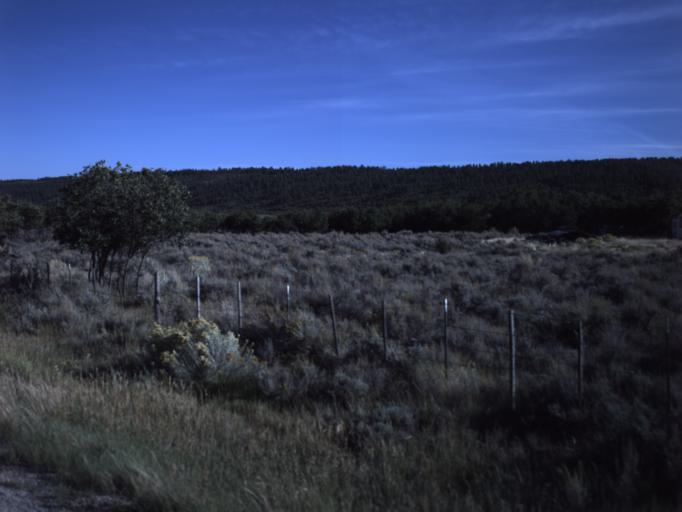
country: US
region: Utah
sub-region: Grand County
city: Moab
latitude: 38.3391
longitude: -109.1669
